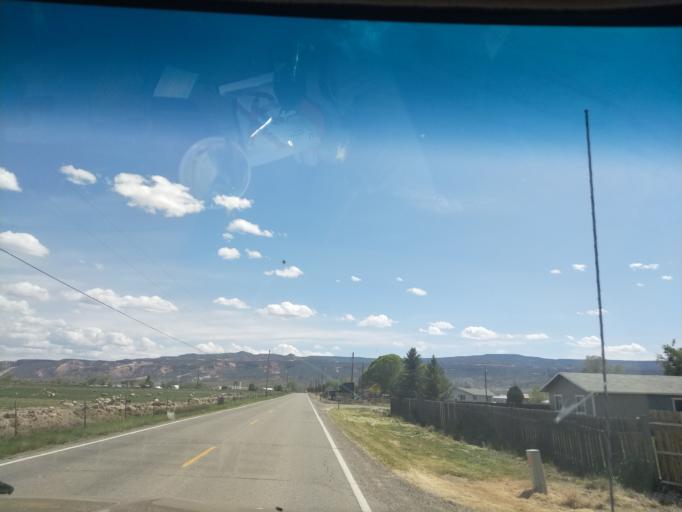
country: US
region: Colorado
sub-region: Mesa County
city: Fruita
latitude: 39.1739
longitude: -108.7571
